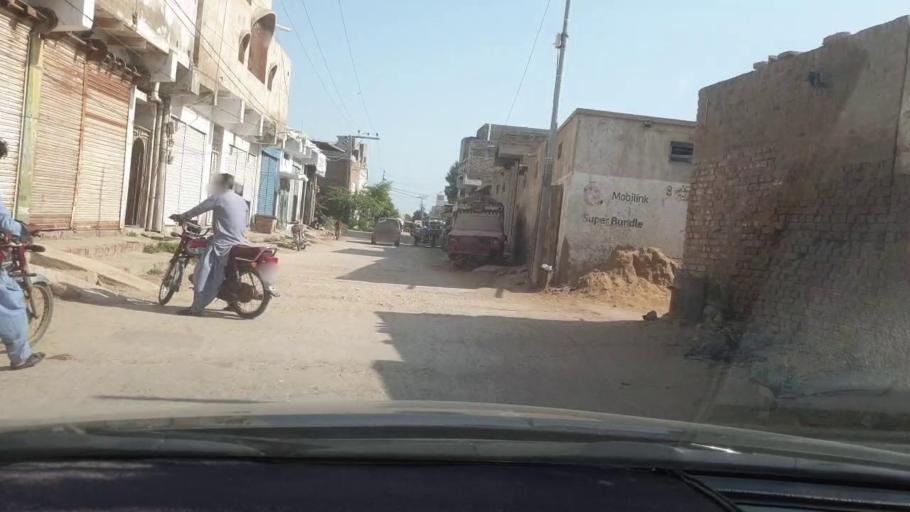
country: PK
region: Sindh
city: Naukot
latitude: 24.7634
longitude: 69.1989
